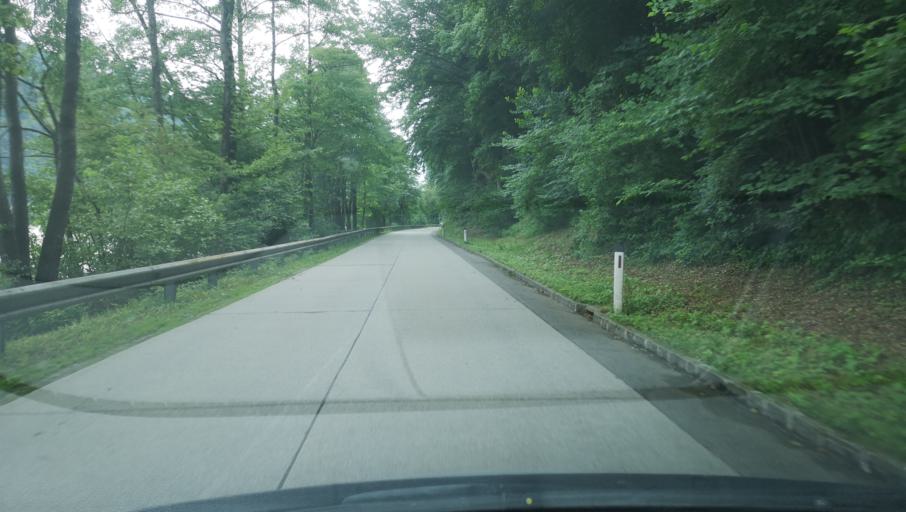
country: AT
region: Lower Austria
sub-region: Politischer Bezirk Melk
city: Nochling
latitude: 48.1938
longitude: 14.9974
